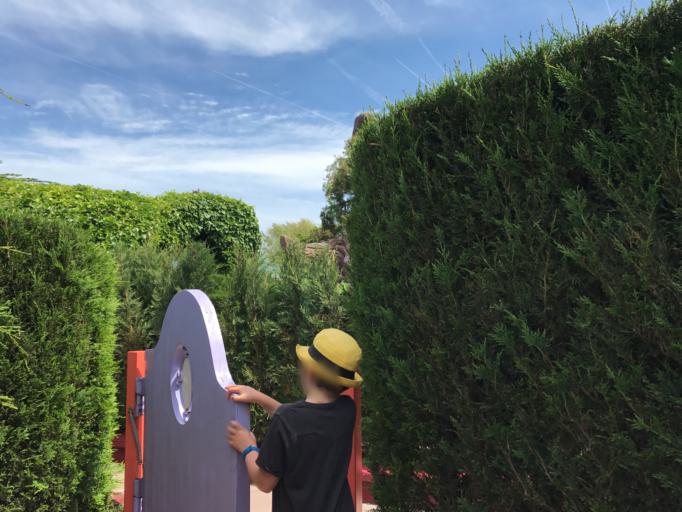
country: FR
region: Ile-de-France
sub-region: Departement de Seine-et-Marne
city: Chessy
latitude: 48.8745
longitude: 2.7742
